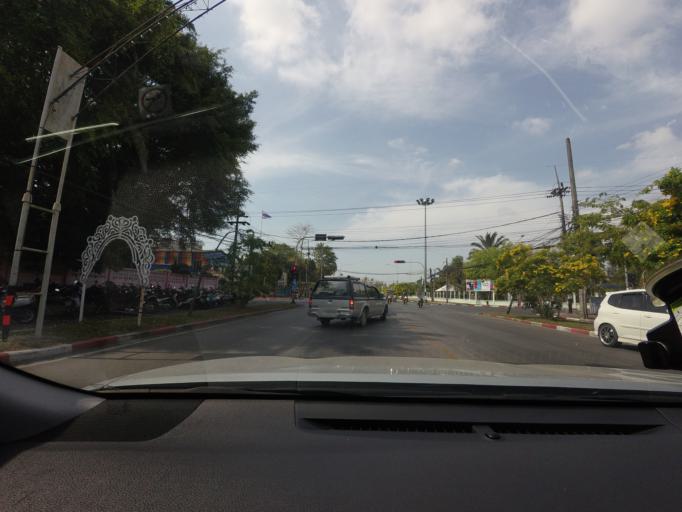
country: TH
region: Yala
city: Yala
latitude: 6.5463
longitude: 101.2837
